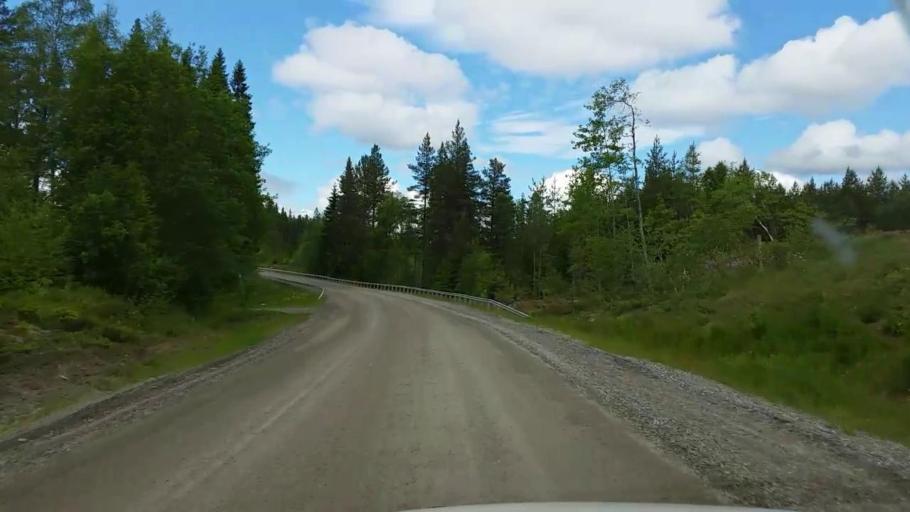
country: SE
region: Gaevleborg
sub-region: Bollnas Kommun
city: Kilafors
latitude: 60.9916
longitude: 16.4051
